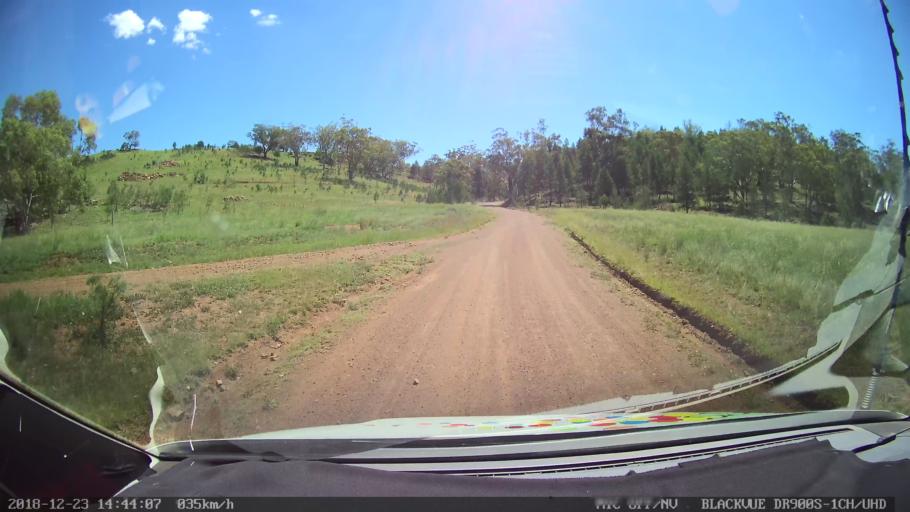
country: AU
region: New South Wales
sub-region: Tamworth Municipality
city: Manilla
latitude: -30.6455
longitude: 150.8975
